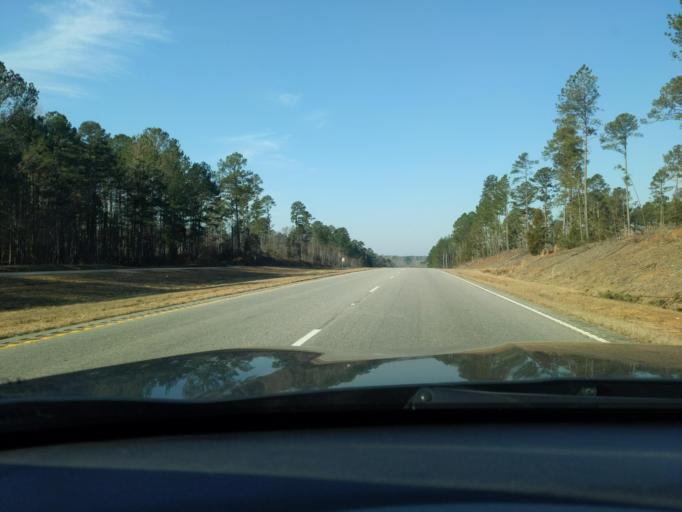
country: US
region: South Carolina
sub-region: Abbeville County
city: Abbeville
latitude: 34.1842
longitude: -82.2942
